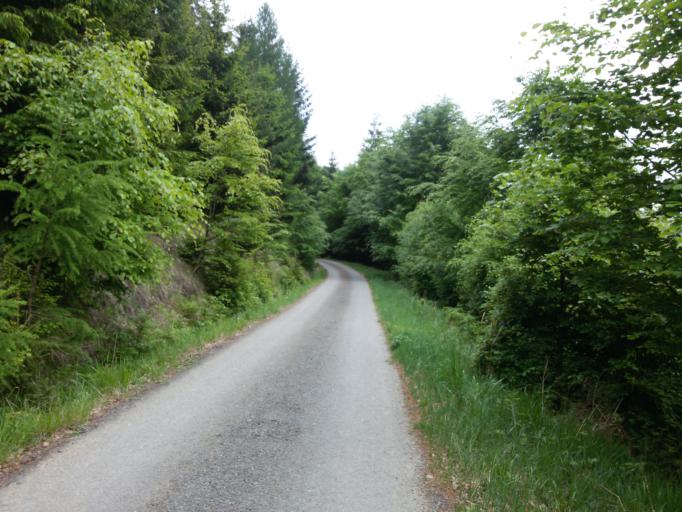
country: CZ
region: Olomoucky
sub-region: Okres Sumperk
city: Loucna nad Desnou
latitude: 50.1094
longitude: 17.1114
